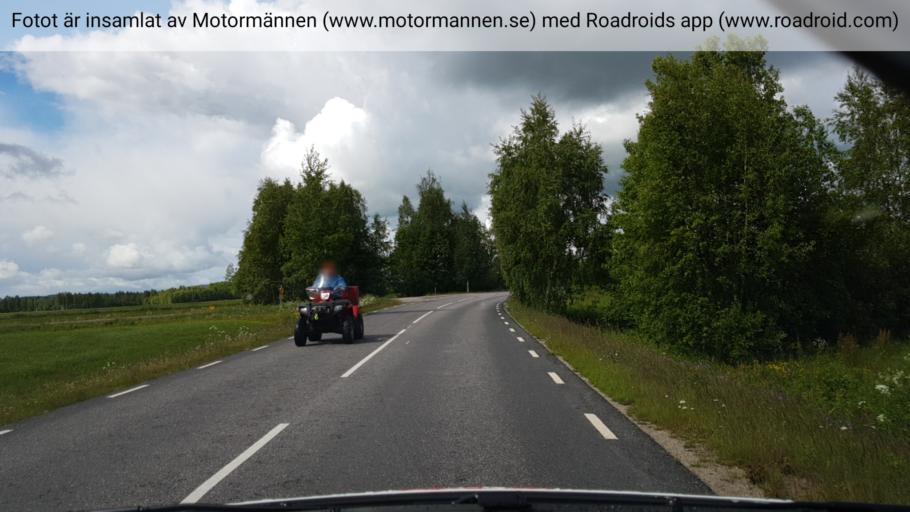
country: SE
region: Vaesterbotten
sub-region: Vannas Kommun
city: Vannasby
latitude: 63.8839
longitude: 19.8884
